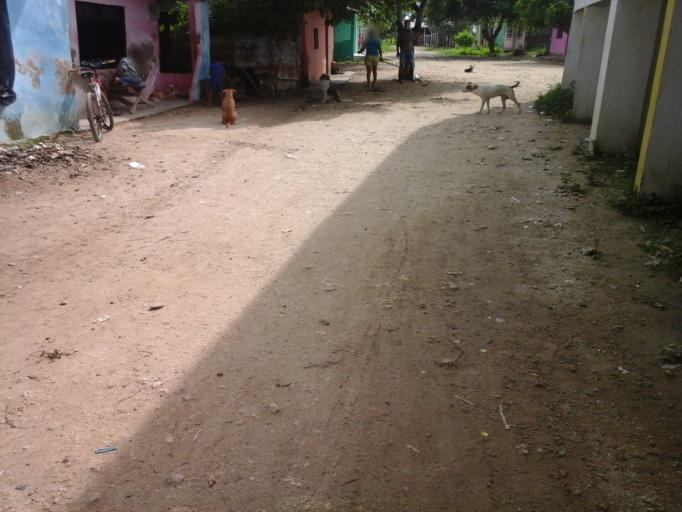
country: CO
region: Bolivar
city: San Pablo
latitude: 10.1431
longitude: -75.2745
